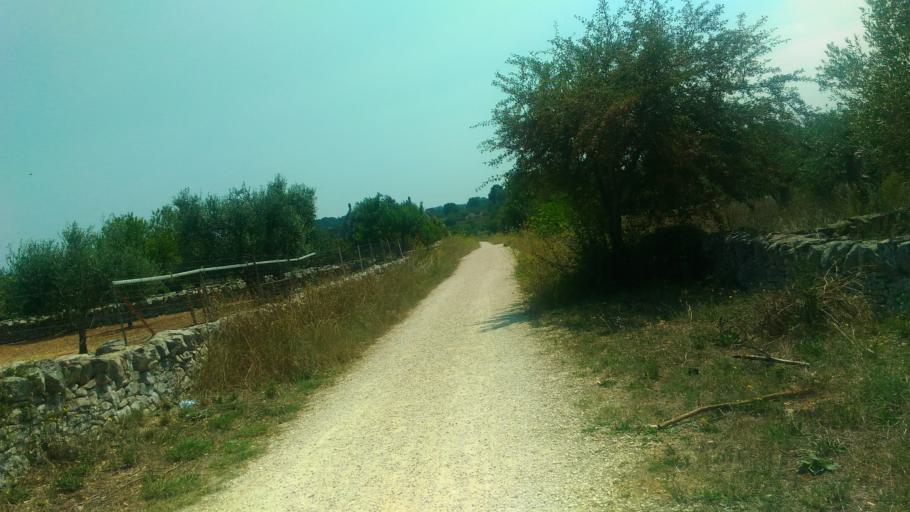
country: IT
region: Apulia
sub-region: Provincia di Brindisi
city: Cisternino
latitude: 40.7393
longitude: 17.3840
